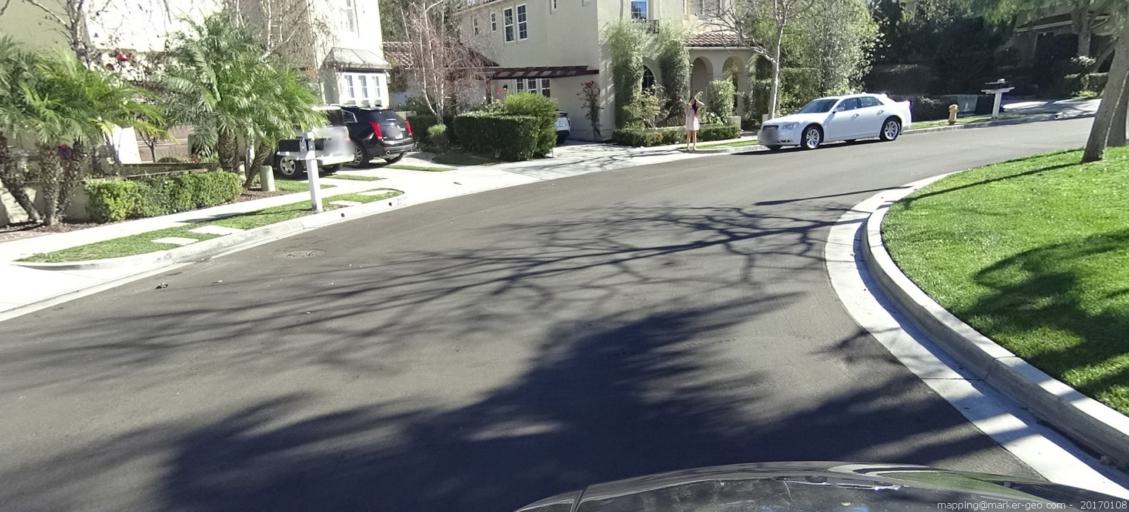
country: US
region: California
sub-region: Orange County
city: Ladera Ranch
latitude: 33.5684
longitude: -117.6331
